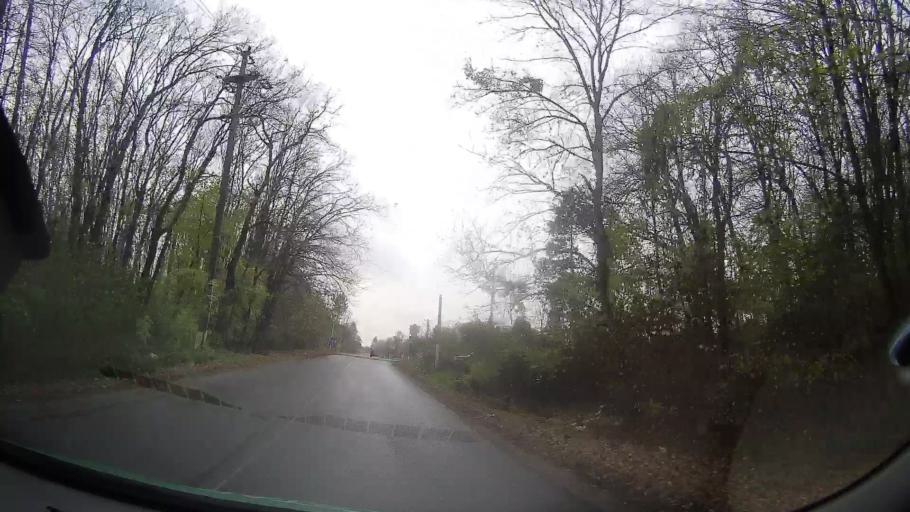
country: RO
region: Ilfov
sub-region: Comuna Snagov
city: Snagov
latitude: 44.7144
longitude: 26.1940
